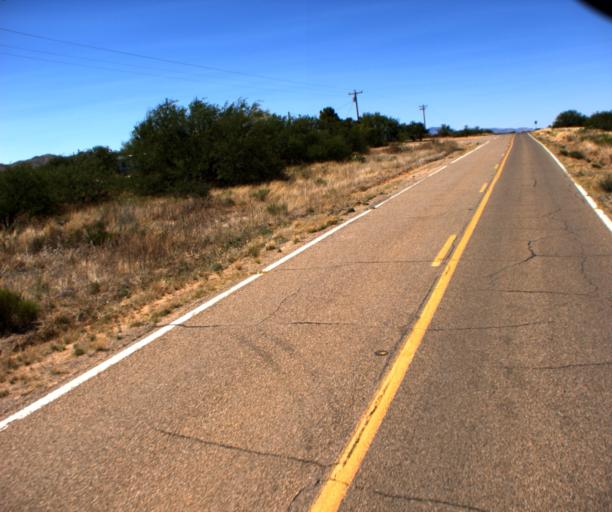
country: US
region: Arizona
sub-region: Santa Cruz County
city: Tubac
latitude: 31.4965
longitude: -111.5461
